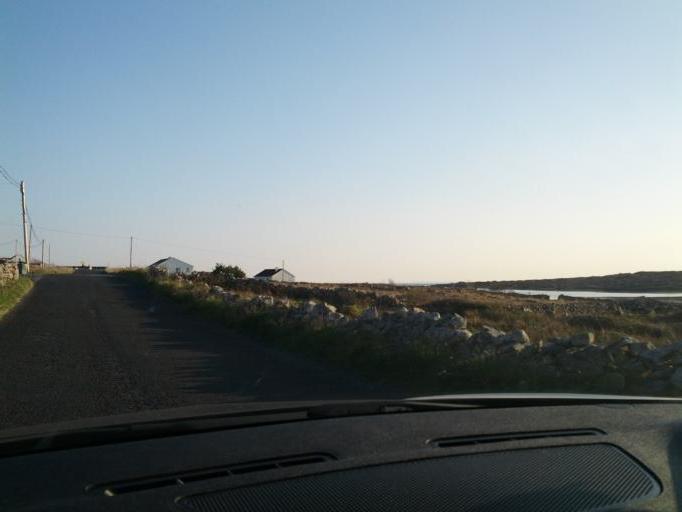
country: IE
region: Connaught
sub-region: County Galway
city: Oughterard
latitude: 53.2621
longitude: -9.5455
